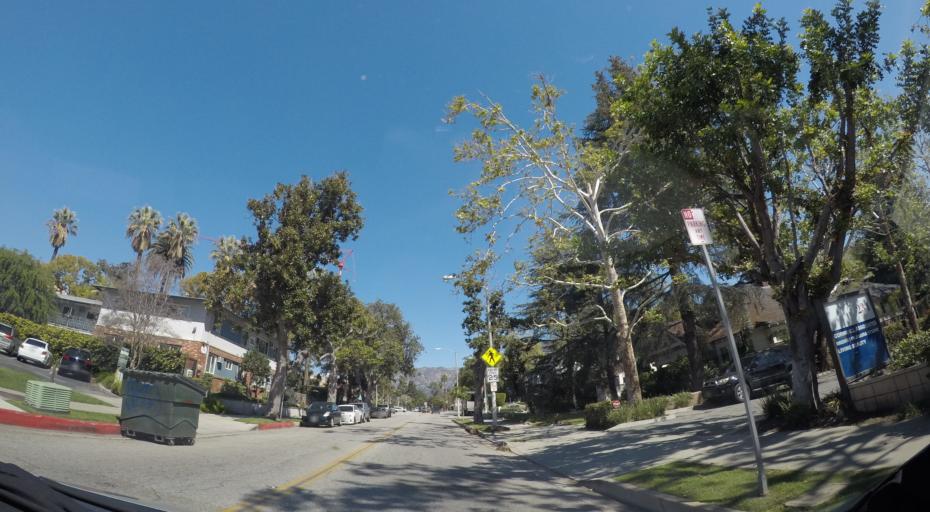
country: US
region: California
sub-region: Los Angeles County
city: Pasadena
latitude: 34.1499
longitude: -118.1369
